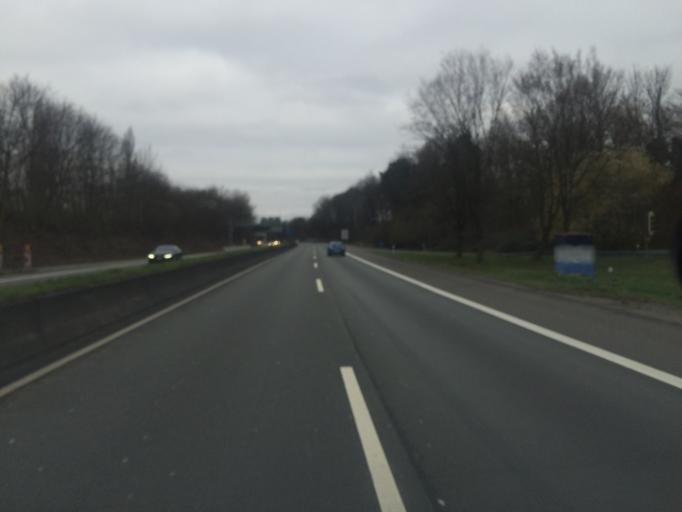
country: DE
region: North Rhine-Westphalia
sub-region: Regierungsbezirk Arnsberg
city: Bochum
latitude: 51.4954
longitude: 7.2317
